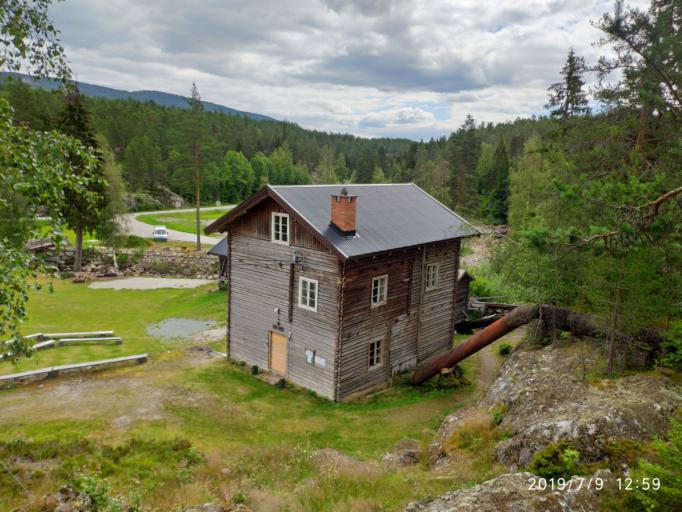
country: NO
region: Buskerud
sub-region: Fla
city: Fla
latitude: 60.2306
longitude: 9.3611
